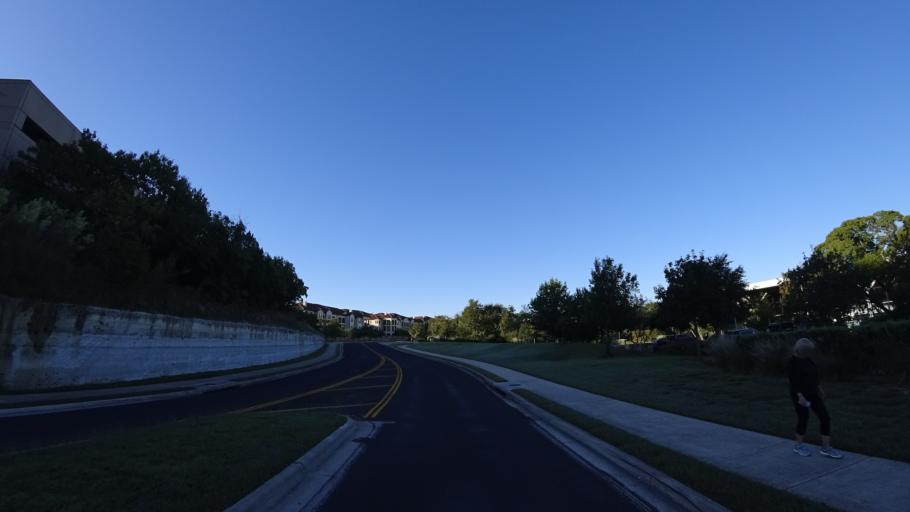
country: US
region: Texas
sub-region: Travis County
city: West Lake Hills
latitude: 30.3354
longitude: -97.8098
